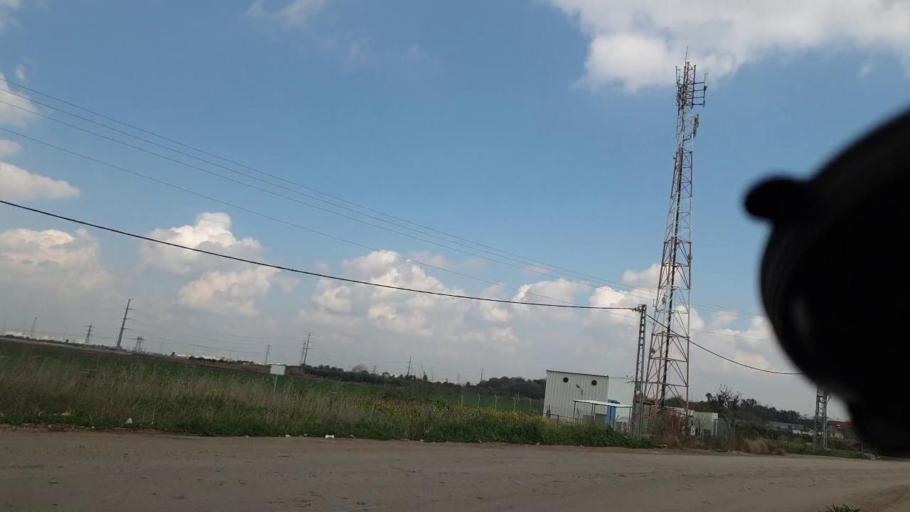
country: IL
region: Haifa
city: Rekhasim
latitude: 32.7546
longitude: 35.0860
